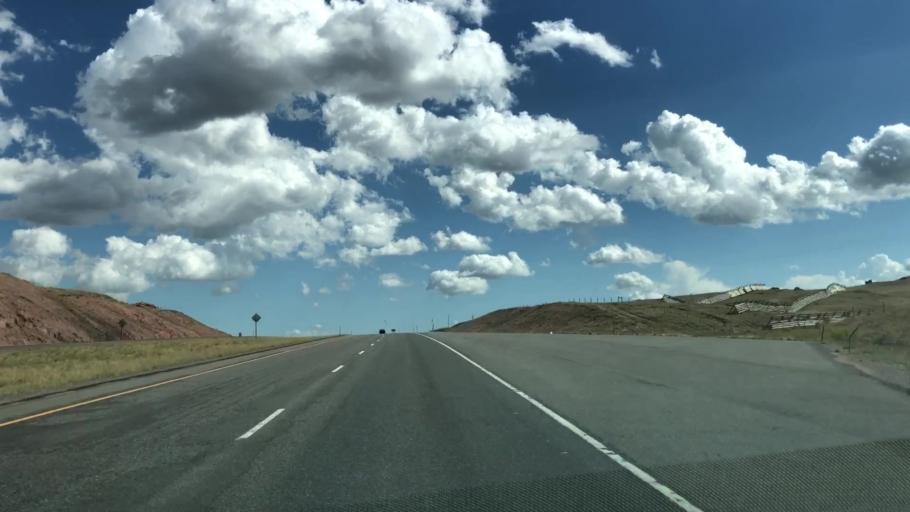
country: US
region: Wyoming
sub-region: Albany County
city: Laramie
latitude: 41.0552
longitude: -105.4712
